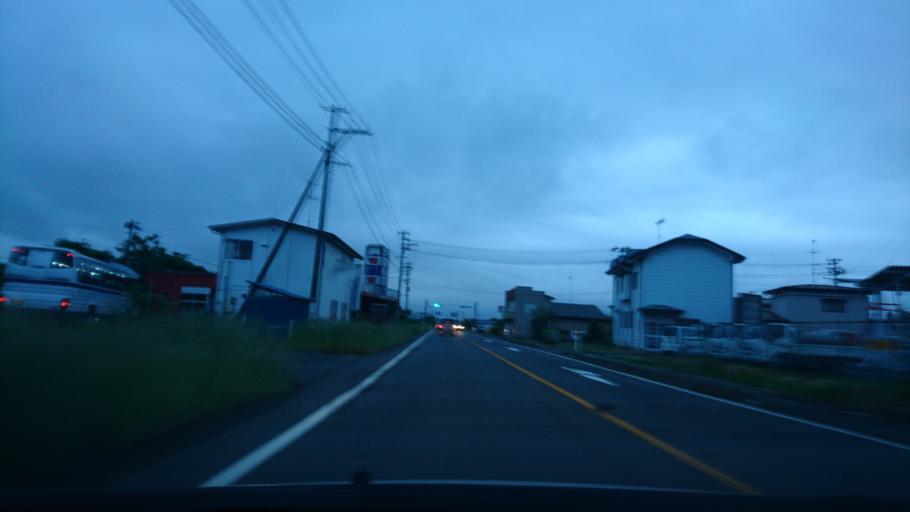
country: JP
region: Iwate
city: Ichinoseki
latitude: 38.8163
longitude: 141.0767
